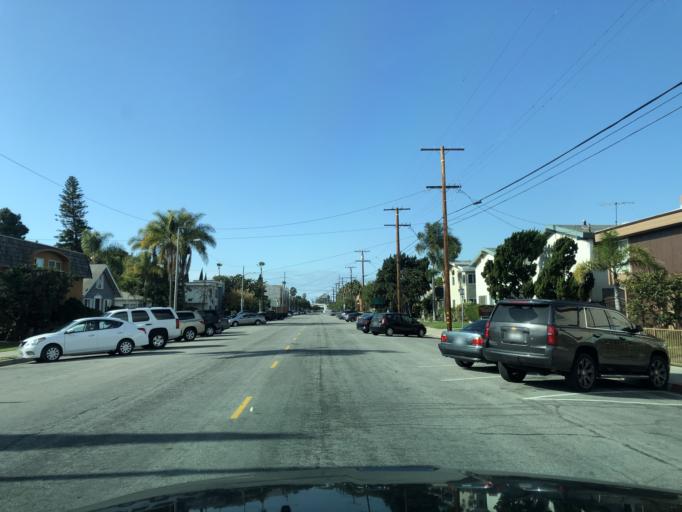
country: US
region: California
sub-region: Los Angeles County
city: Inglewood
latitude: 33.9643
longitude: -118.3625
